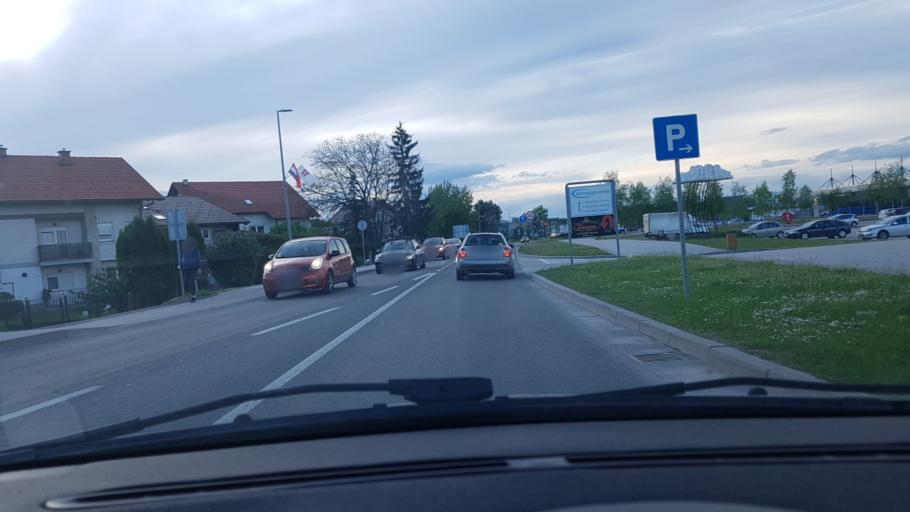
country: HR
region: Zagrebacka
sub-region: Grad Samobor
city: Samobor
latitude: 45.8074
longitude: 15.7163
